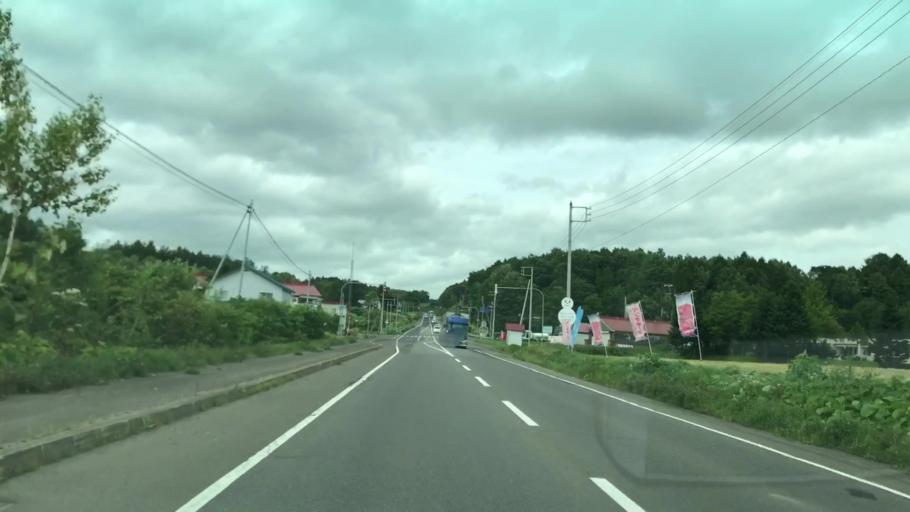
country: JP
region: Hokkaido
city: Niseko Town
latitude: 42.9212
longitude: 140.7400
